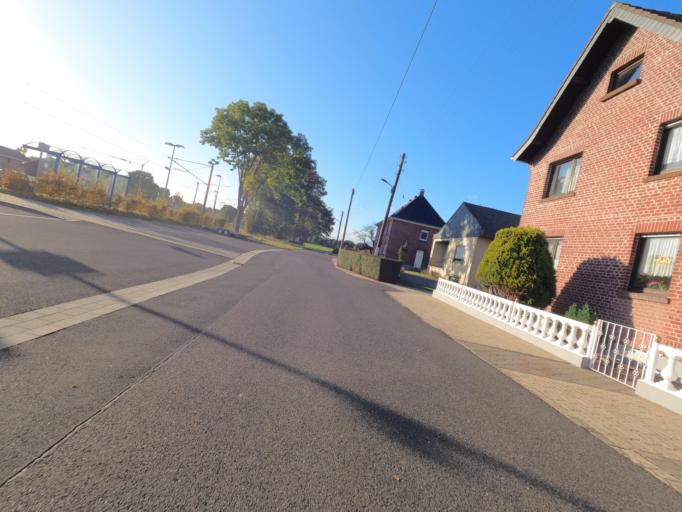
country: DE
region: North Rhine-Westphalia
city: Huckelhoven
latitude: 51.0412
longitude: 6.1732
